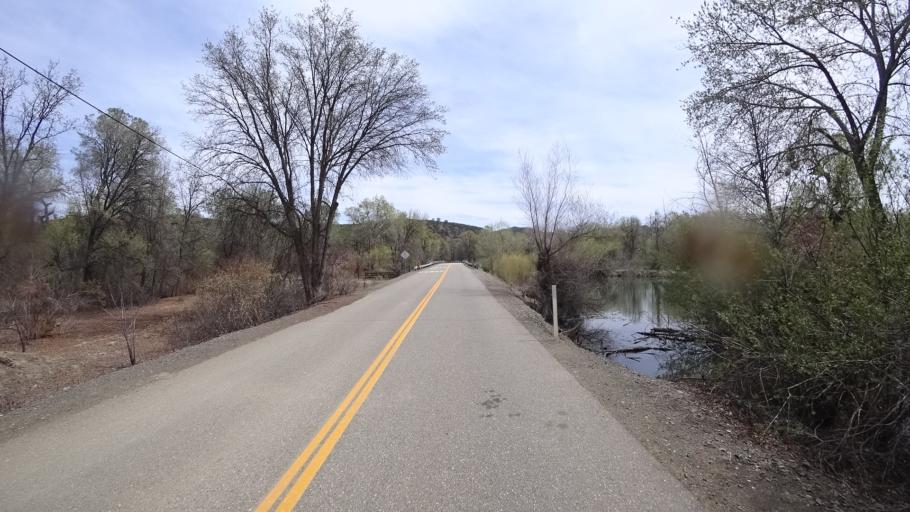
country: US
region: California
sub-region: Glenn County
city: Willows
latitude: 39.4346
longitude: -122.5046
